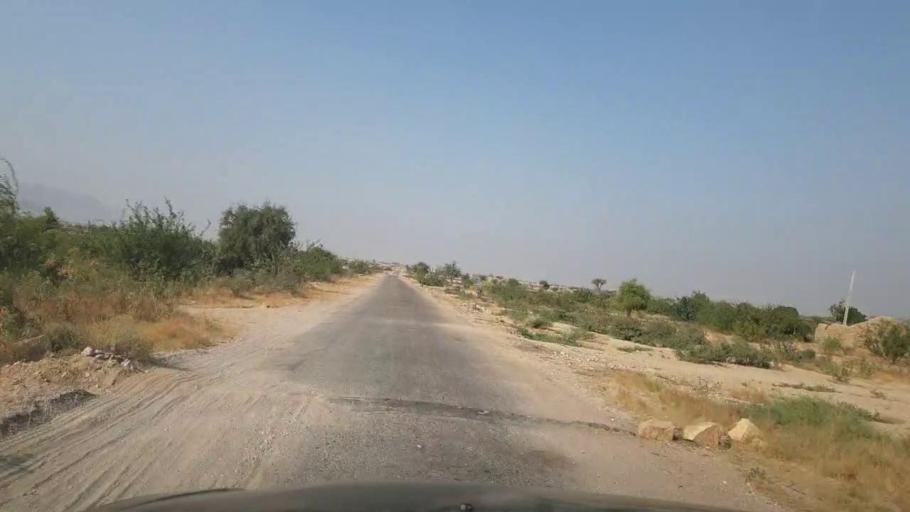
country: PK
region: Sindh
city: Jamshoro
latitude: 25.5922
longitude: 67.8183
